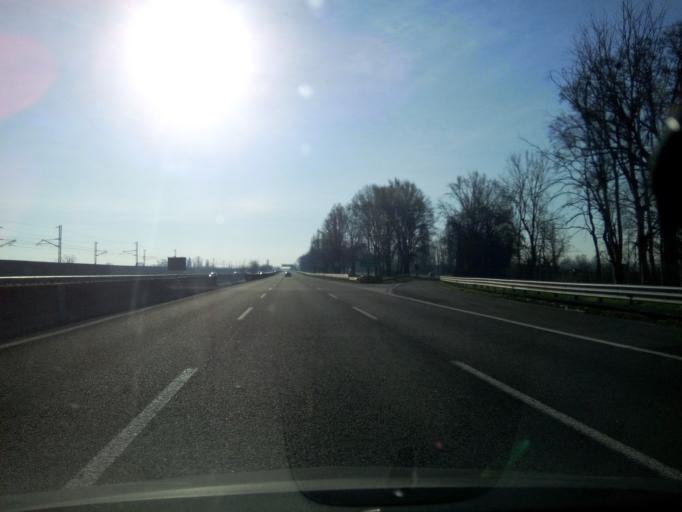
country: IT
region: Emilia-Romagna
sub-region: Provincia di Modena
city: Campogalliano
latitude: 44.6786
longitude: 10.8126
